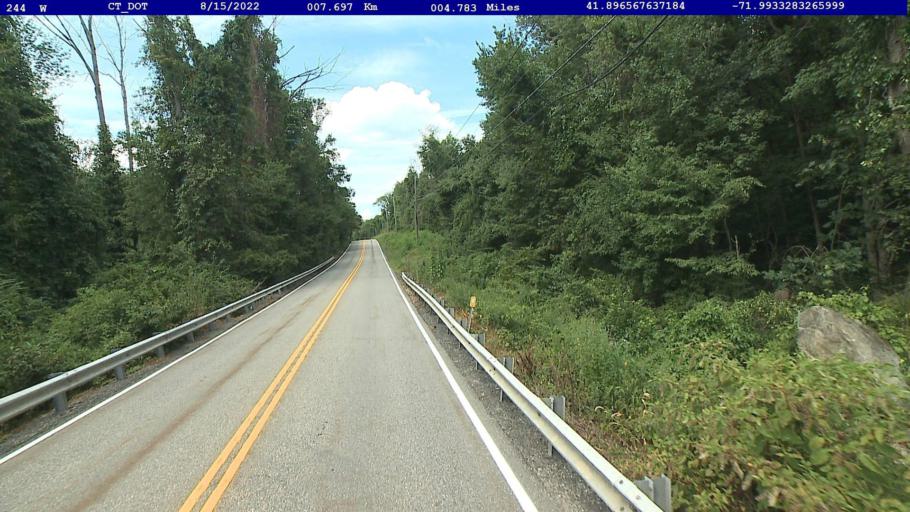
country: US
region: Connecticut
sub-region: Windham County
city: South Woodstock
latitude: 41.8971
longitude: -71.9931
